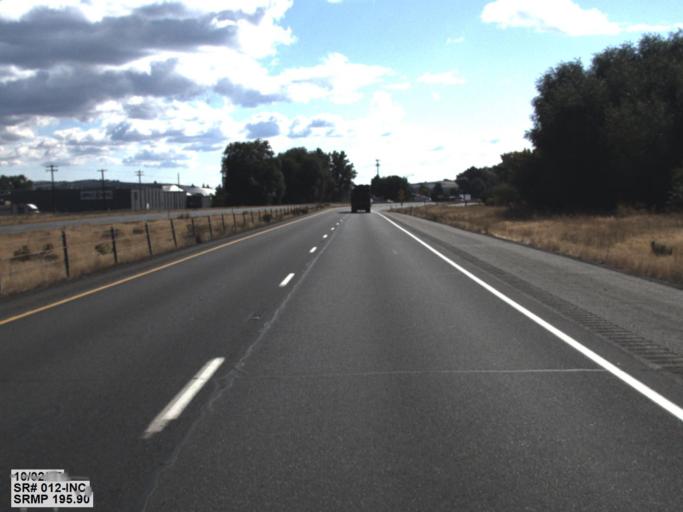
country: US
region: Washington
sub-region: Yakima County
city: Gleed
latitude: 46.6634
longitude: -120.6233
